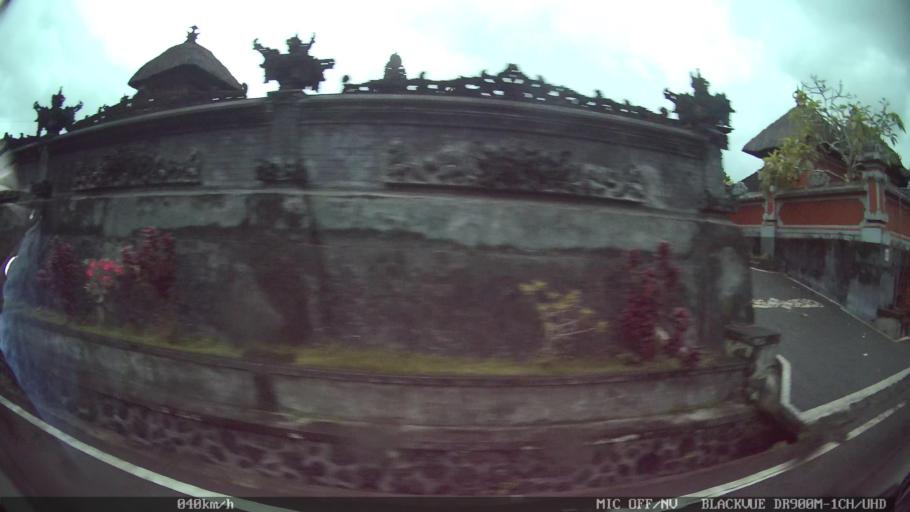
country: ID
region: Bali
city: Banjar Serangan
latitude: -8.5426
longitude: 115.1835
